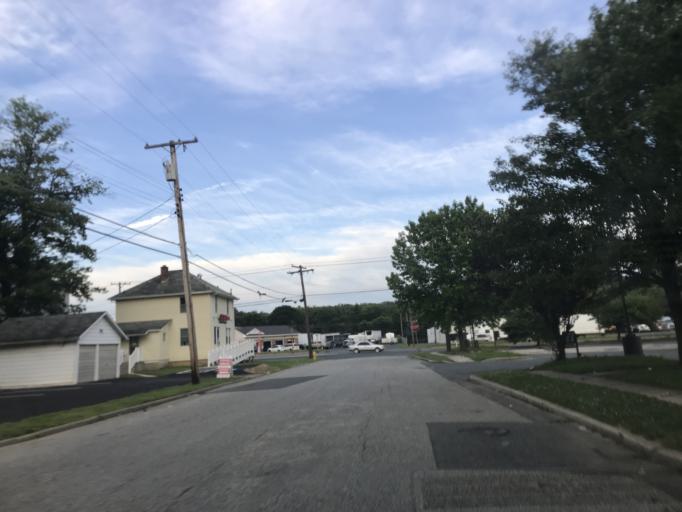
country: US
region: Maryland
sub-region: Harford County
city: Aberdeen
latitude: 39.5017
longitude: -76.1695
